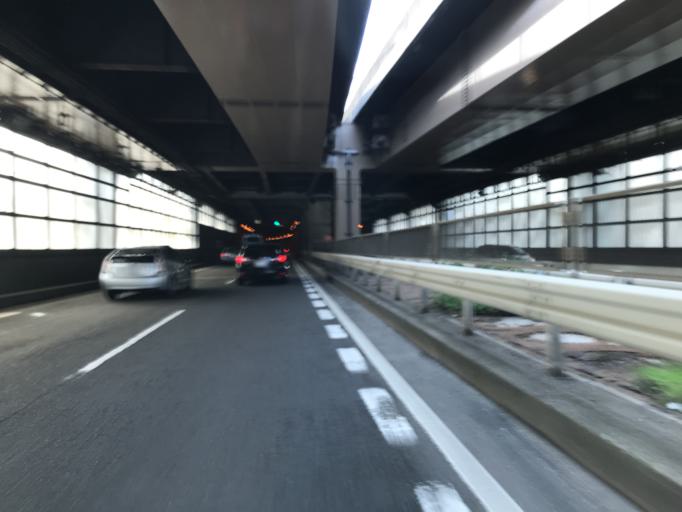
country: JP
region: Miyagi
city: Sendai
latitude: 38.2616
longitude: 140.8594
